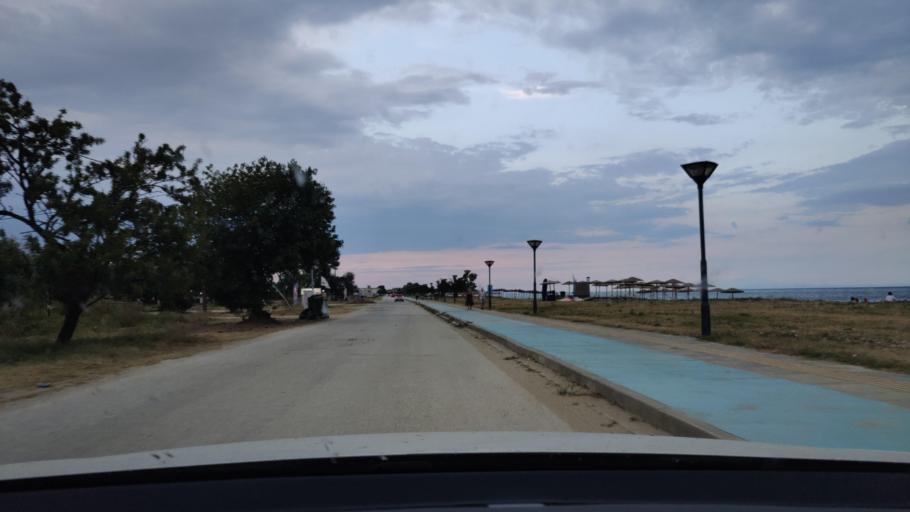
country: GR
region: East Macedonia and Thrace
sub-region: Nomos Kavalas
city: Paralia Ofryniou
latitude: 40.7699
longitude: 23.8902
